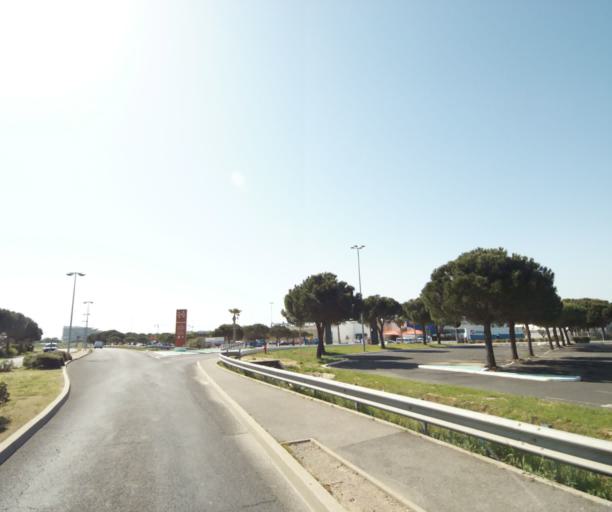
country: FR
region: Languedoc-Roussillon
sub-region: Departement de l'Herault
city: Perols
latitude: 43.5850
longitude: 3.9302
